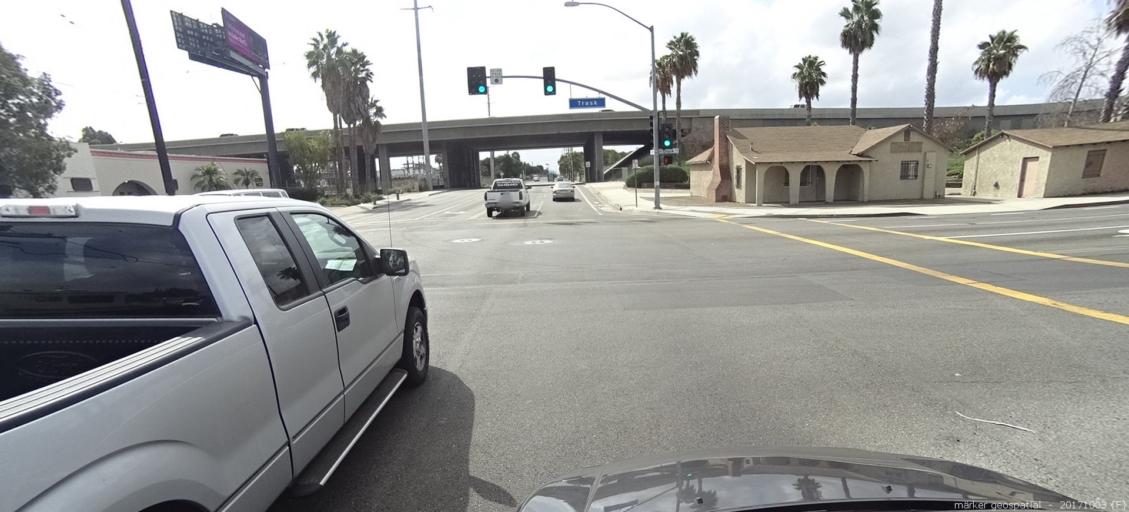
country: US
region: California
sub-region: Orange County
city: Garden Grove
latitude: 33.7672
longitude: -117.9291
